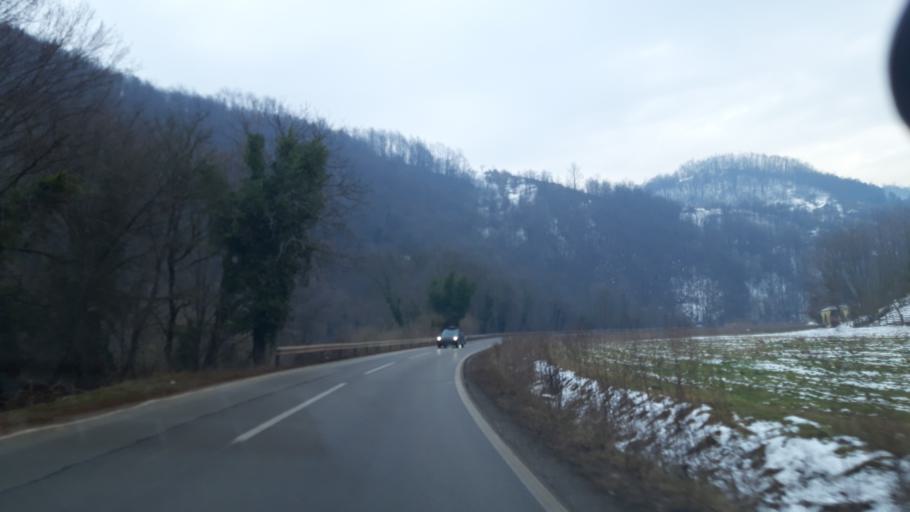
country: BA
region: Republika Srpska
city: Milici
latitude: 44.1874
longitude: 19.0743
